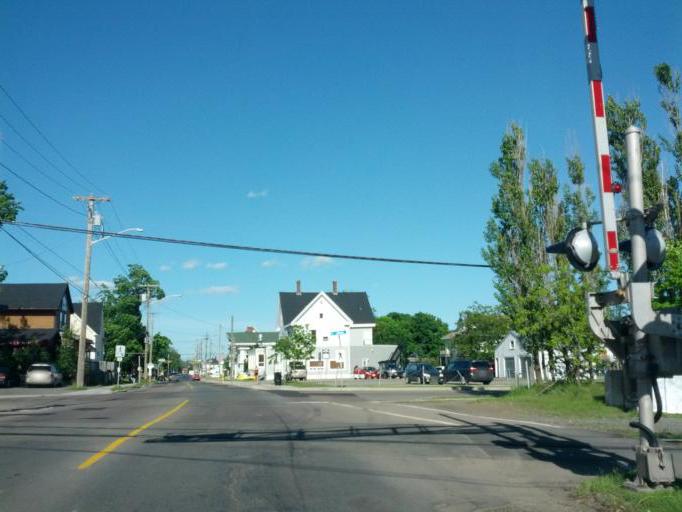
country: CA
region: New Brunswick
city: Moncton
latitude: 46.0918
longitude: -64.7799
